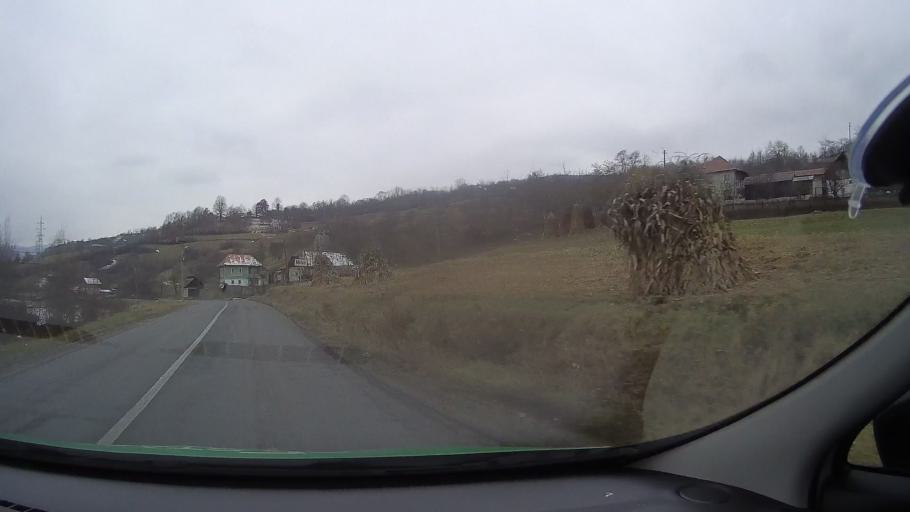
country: RO
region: Alba
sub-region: Comuna Metes
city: Metes
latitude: 46.1038
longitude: 23.4377
